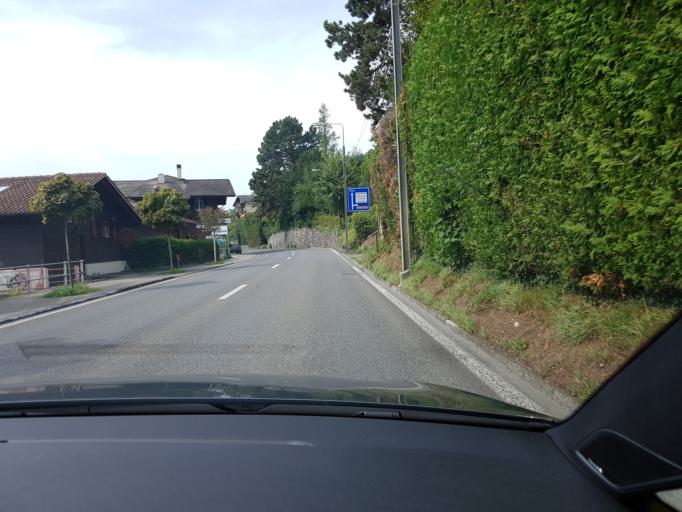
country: CH
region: Bern
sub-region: Thun District
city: Hilterfingen
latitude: 46.7238
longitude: 7.6826
